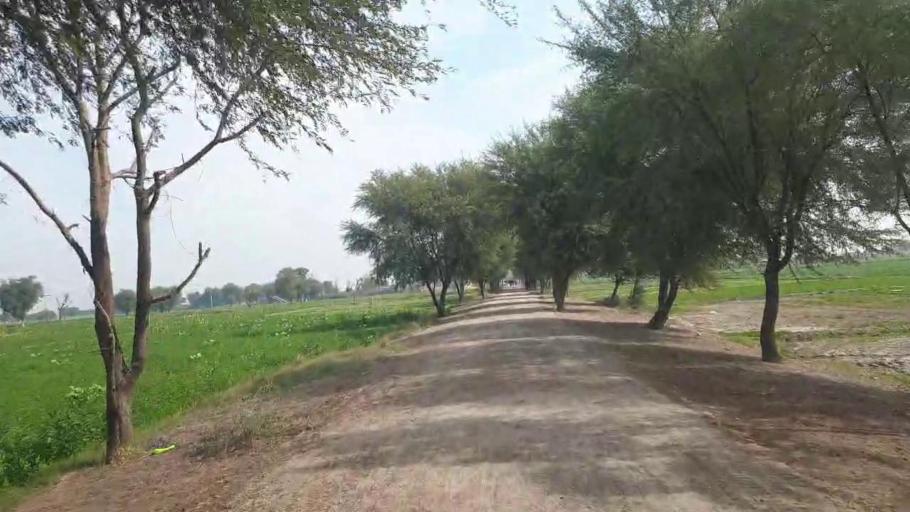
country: PK
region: Sindh
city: Nawabshah
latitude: 26.1280
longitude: 68.4927
